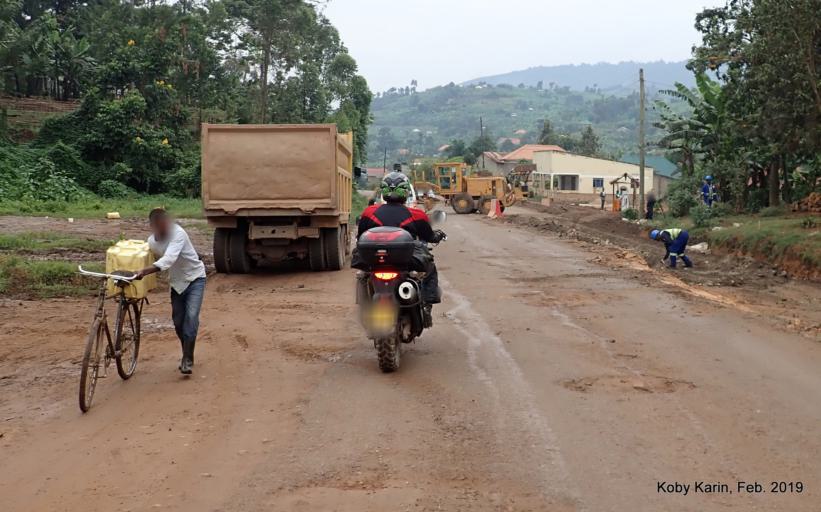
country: UG
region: Western Region
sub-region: Rubirizi District
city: Rubirizi
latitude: -0.2869
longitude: 30.1048
